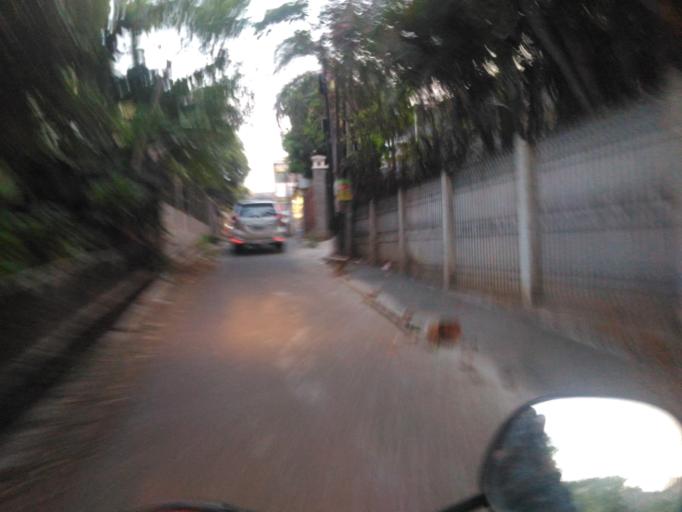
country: ID
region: West Java
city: Depok
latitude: -6.3639
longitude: 106.8362
